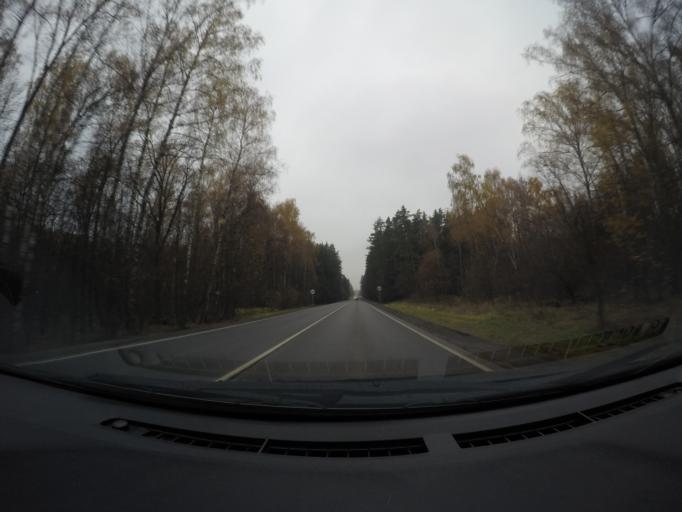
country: RU
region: Moskovskaya
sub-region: Podol'skiy Rayon
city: Podol'sk
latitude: 55.3781
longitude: 37.6373
